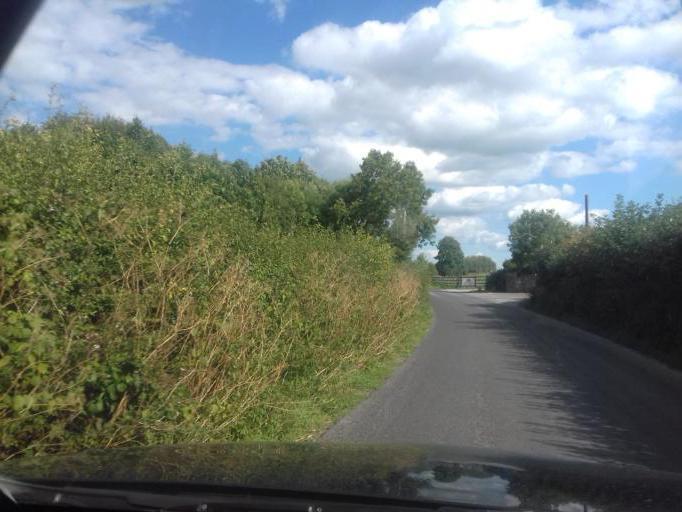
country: IE
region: Leinster
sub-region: Kilkenny
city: Kilkenny
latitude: 52.5389
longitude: -7.2532
